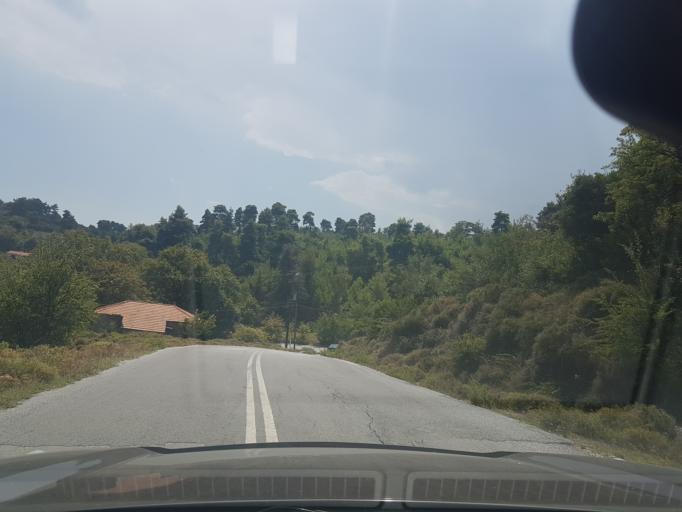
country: GR
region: Central Greece
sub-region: Nomos Evvoias
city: Kymi
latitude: 38.6361
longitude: 24.0739
